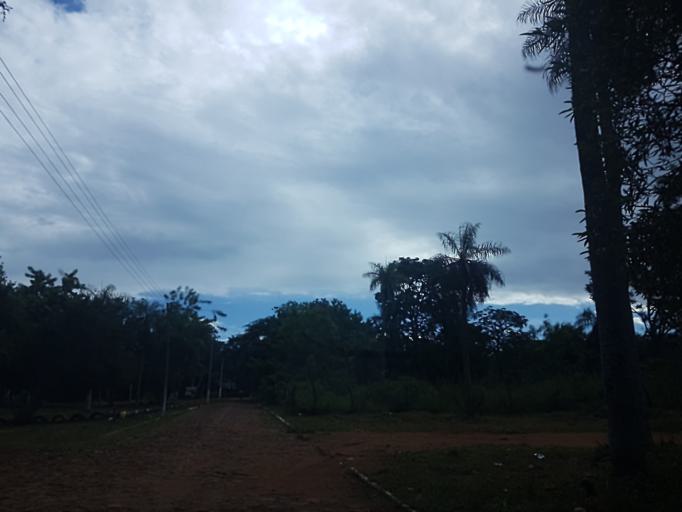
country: PY
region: Central
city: Limpio
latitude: -25.2386
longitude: -57.4454
